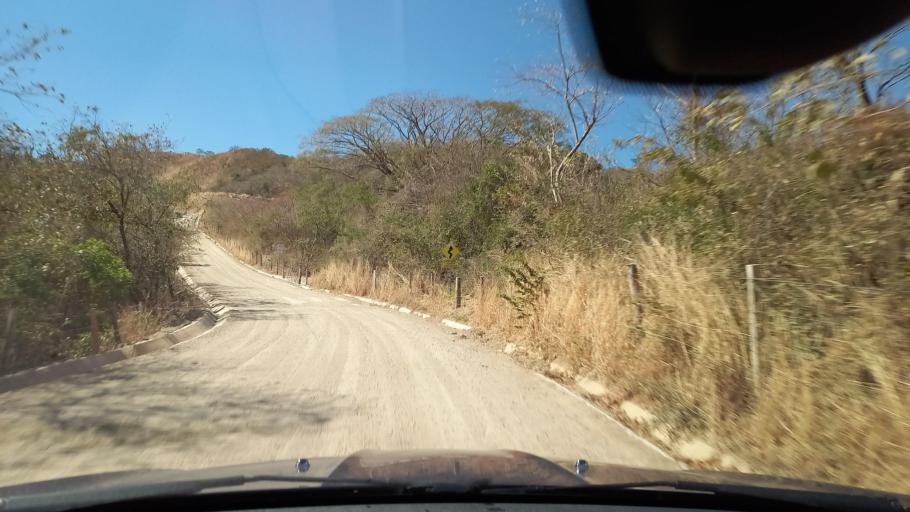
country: SV
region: Santa Ana
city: Metapan
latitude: 14.3595
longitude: -89.4769
